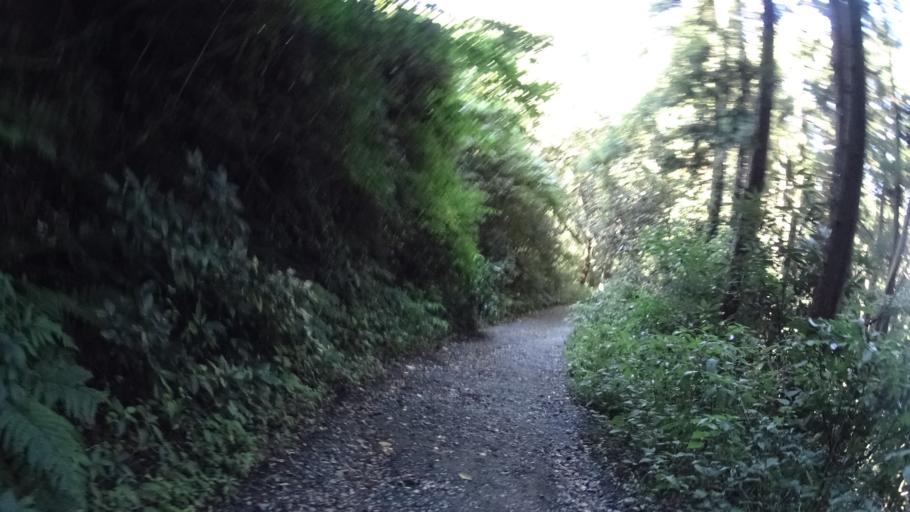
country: JP
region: Kanagawa
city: Hayama
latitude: 35.2844
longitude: 139.6065
